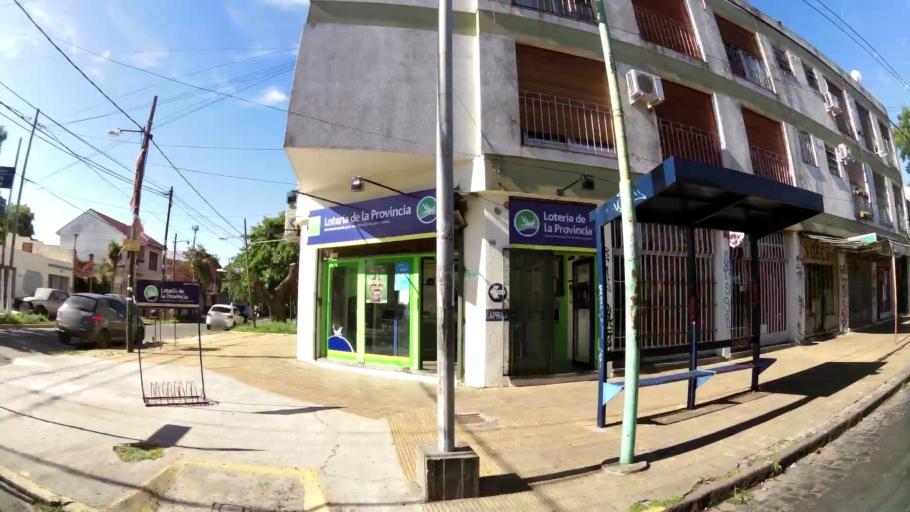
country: AR
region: Buenos Aires
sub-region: Partido de Lomas de Zamora
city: Lomas de Zamora
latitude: -34.7582
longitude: -58.4186
